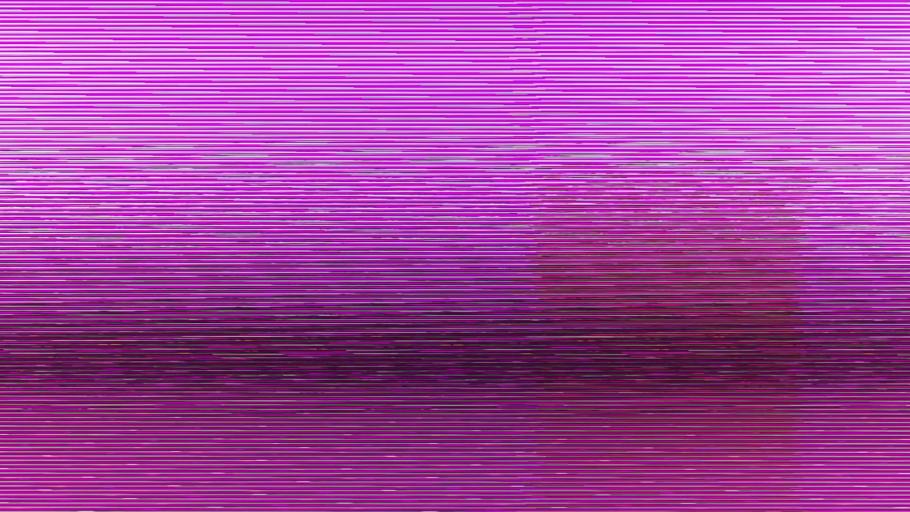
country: US
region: Michigan
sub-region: Macomb County
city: Shelby
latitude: 42.7115
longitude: -83.0263
